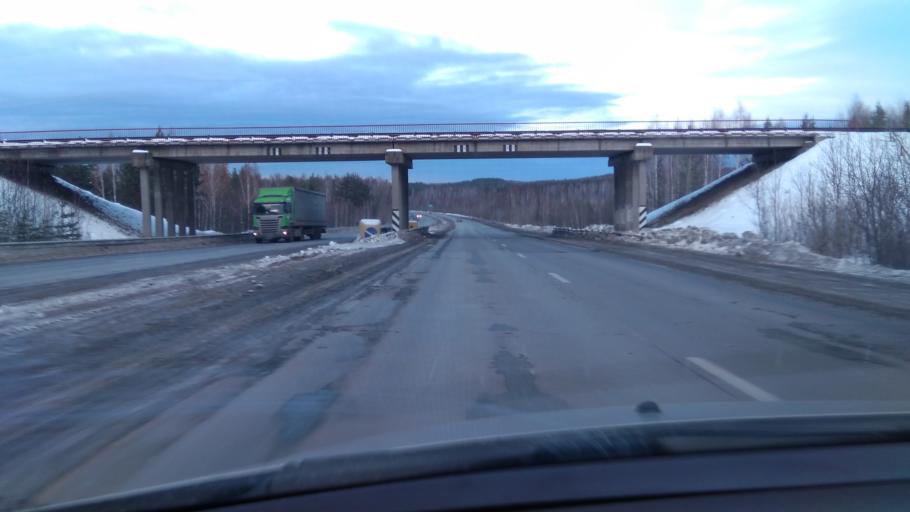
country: RU
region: Sverdlovsk
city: Shchelkun
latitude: 56.3176
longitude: 60.8694
